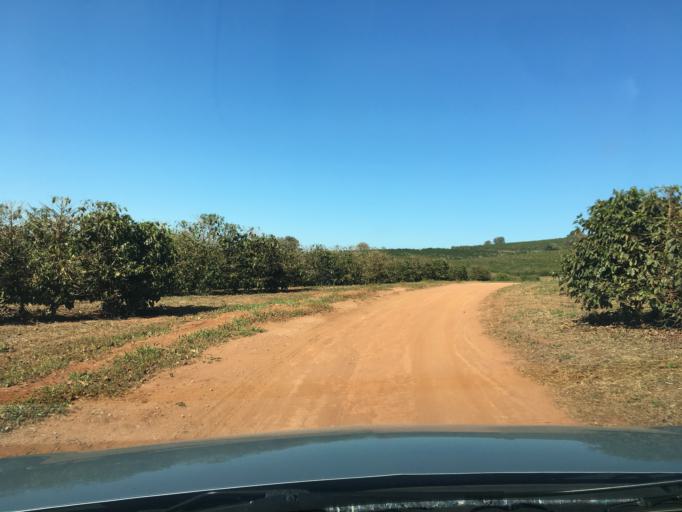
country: BR
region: Minas Gerais
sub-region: Campestre
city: Campestre
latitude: -21.5860
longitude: -46.2063
